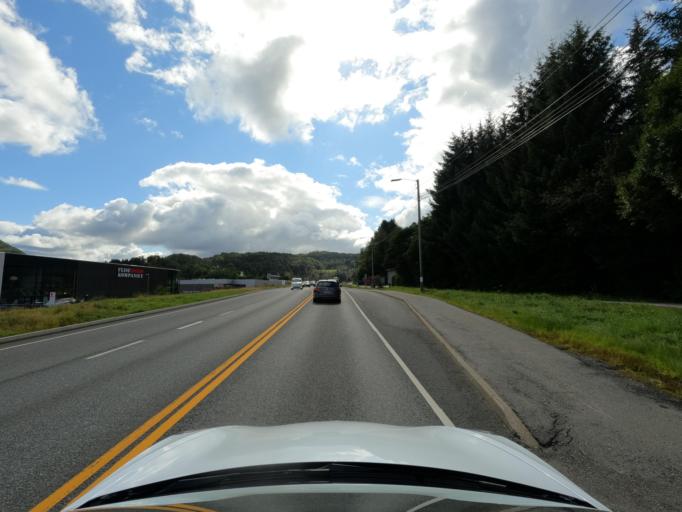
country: NO
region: Hordaland
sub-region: Bergen
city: Hylkje
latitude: 60.4871
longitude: 5.3765
